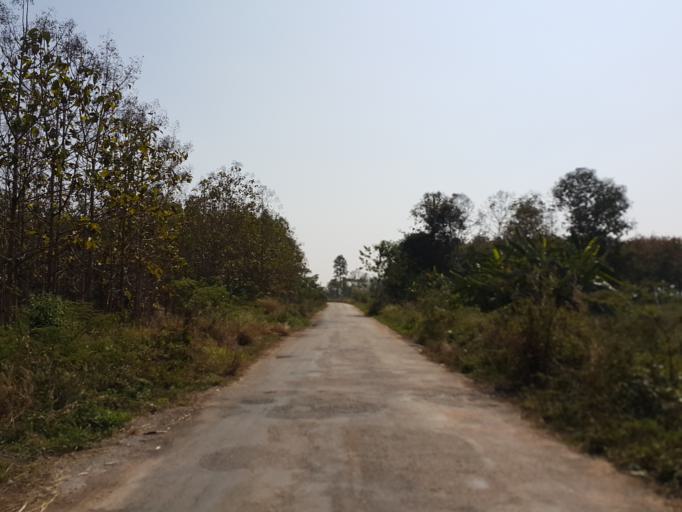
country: TH
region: Lampang
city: Wang Nuea
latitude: 19.0162
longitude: 99.6232
